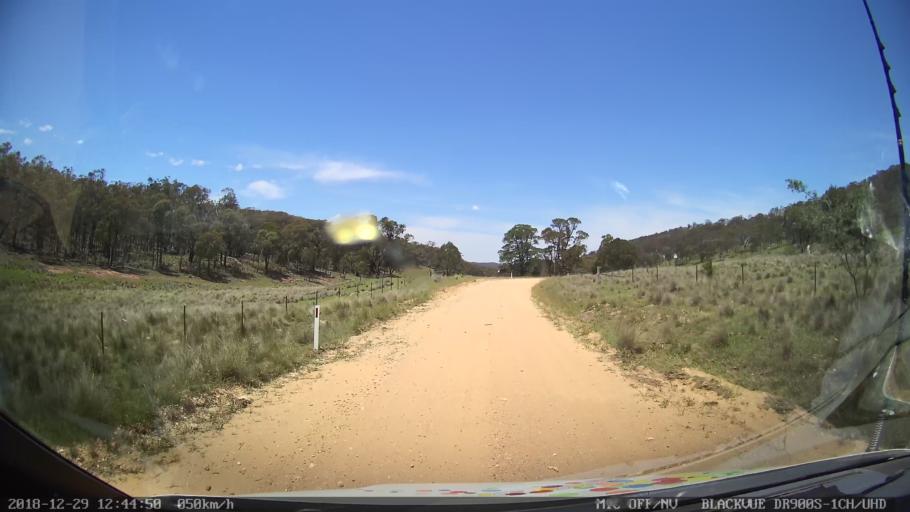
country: AU
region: Australian Capital Territory
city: Macarthur
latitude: -35.6305
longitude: 149.2157
